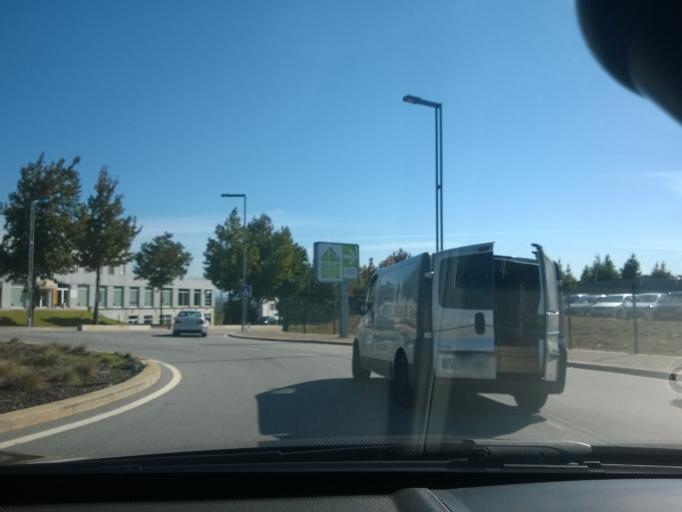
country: PT
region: Porto
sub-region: Maia
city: Anta
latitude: 41.2598
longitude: -8.6366
